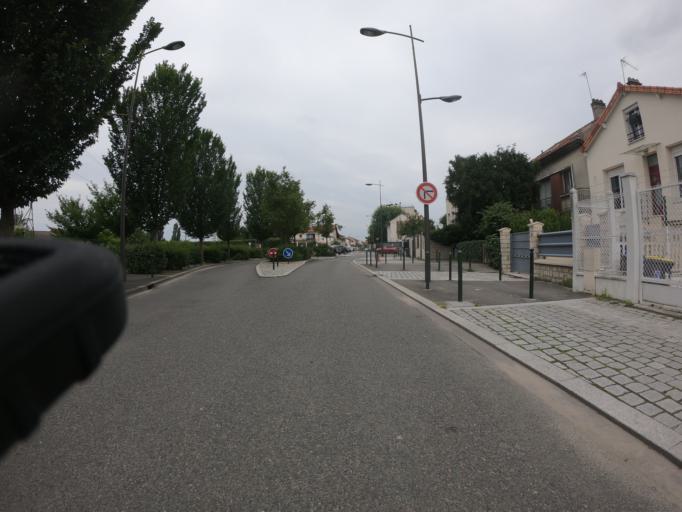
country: FR
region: Ile-de-France
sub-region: Departement du Val-de-Marne
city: Thiais
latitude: 48.7600
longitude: 2.3870
